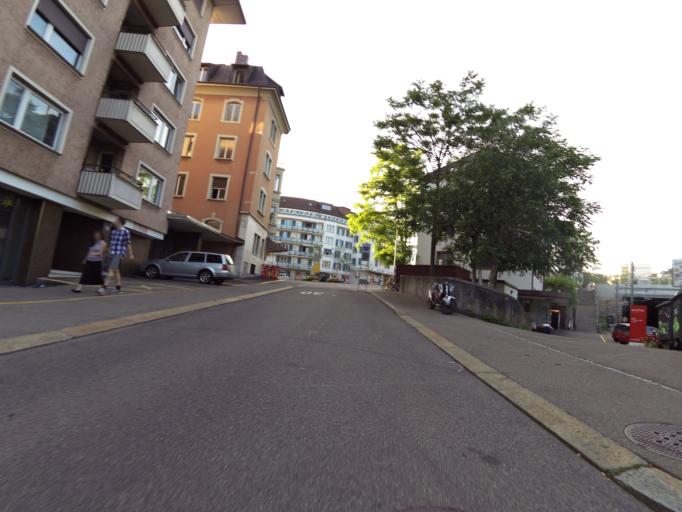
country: CH
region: Zurich
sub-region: Bezirk Zuerich
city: Zuerich (Kreis 10) / Wipkingen
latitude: 47.3927
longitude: 8.5293
